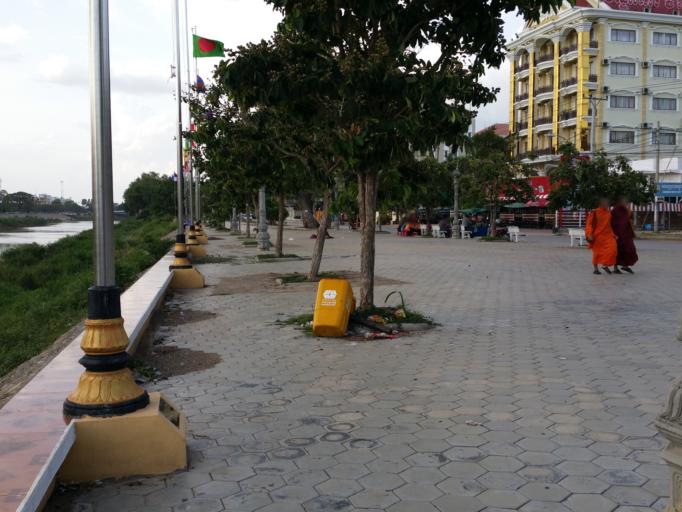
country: KH
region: Battambang
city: Battambang
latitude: 13.0977
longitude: 103.2000
